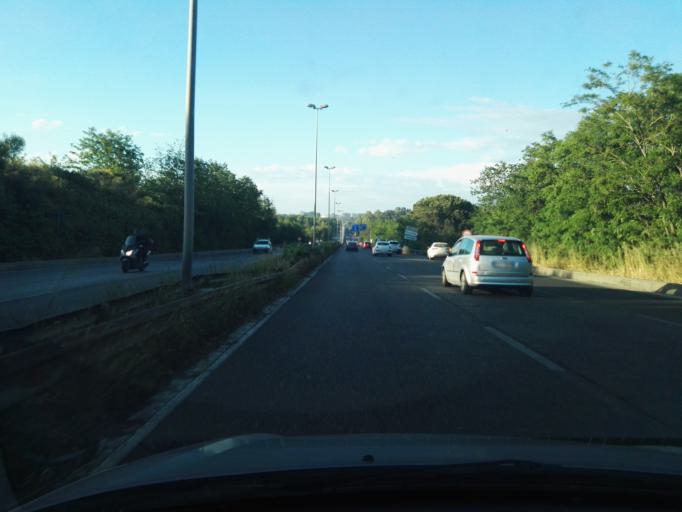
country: IT
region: Latium
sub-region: Citta metropolitana di Roma Capitale
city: Selcetta
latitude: 41.8051
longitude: 12.4553
